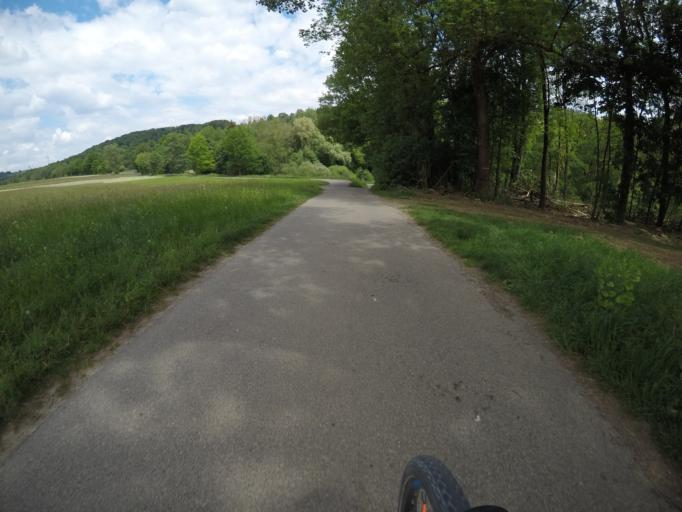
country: DE
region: Baden-Wuerttemberg
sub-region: Regierungsbezirk Stuttgart
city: Ostfildern
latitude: 48.7201
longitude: 9.2177
